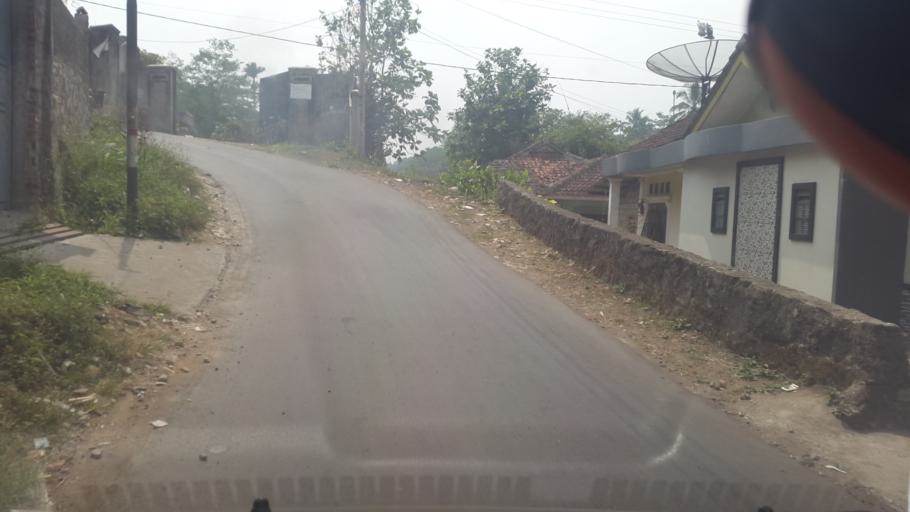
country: ID
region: West Java
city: Sukabumi
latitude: -6.8974
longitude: 106.8753
